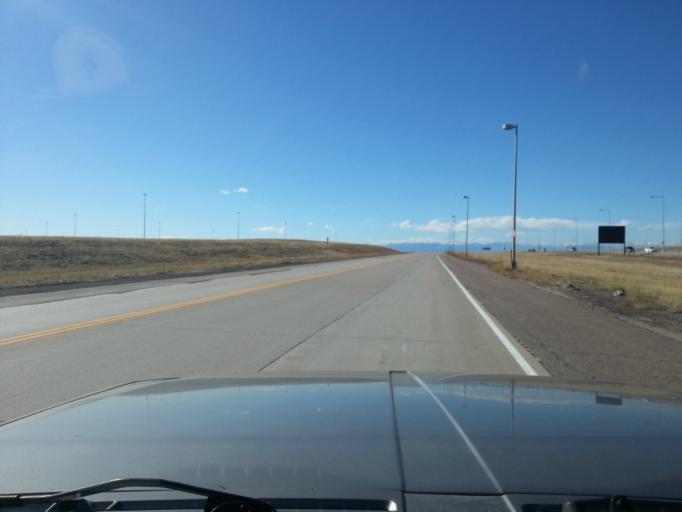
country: US
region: Colorado
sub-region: Adams County
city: Aurora
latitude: 39.8331
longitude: -104.7062
